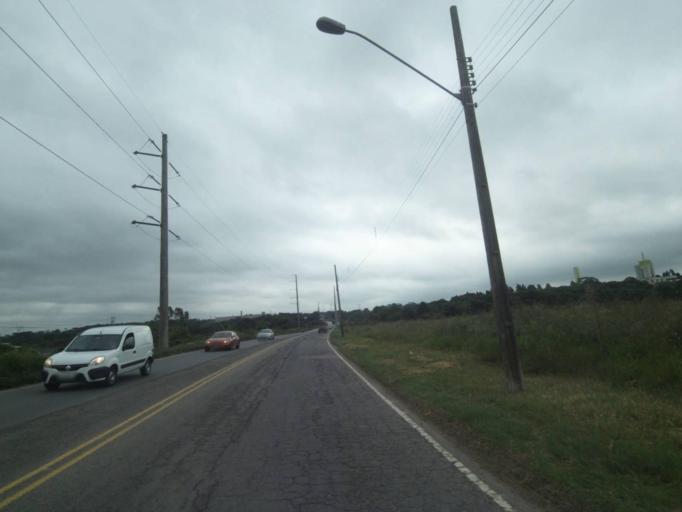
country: BR
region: Parana
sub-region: Araucaria
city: Araucaria
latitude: -25.5265
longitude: -49.3383
